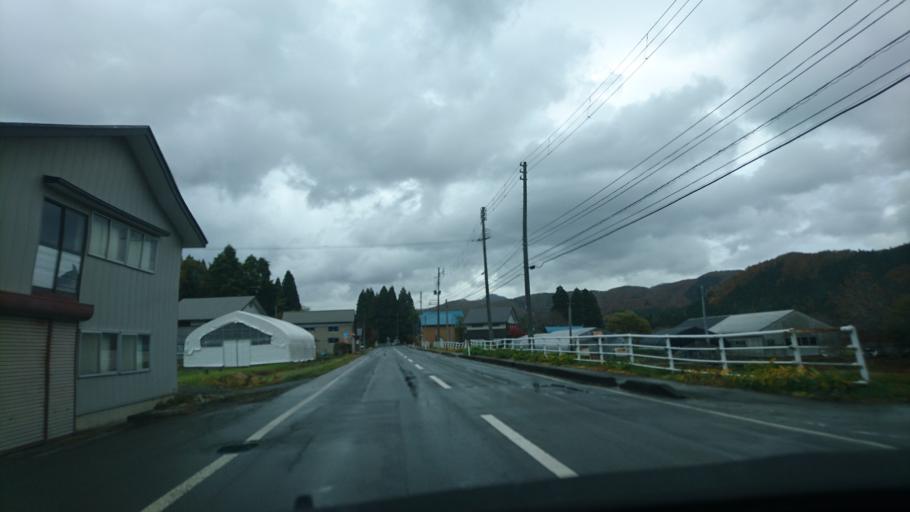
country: JP
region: Akita
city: Kakunodatemachi
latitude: 39.4897
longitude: 140.8095
